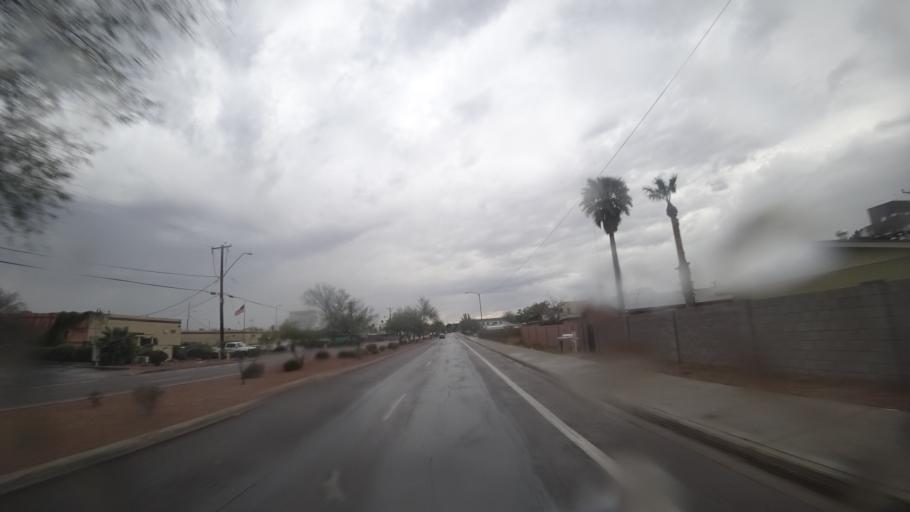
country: US
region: Arizona
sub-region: Maricopa County
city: Tempe
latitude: 33.4405
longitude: -111.9206
